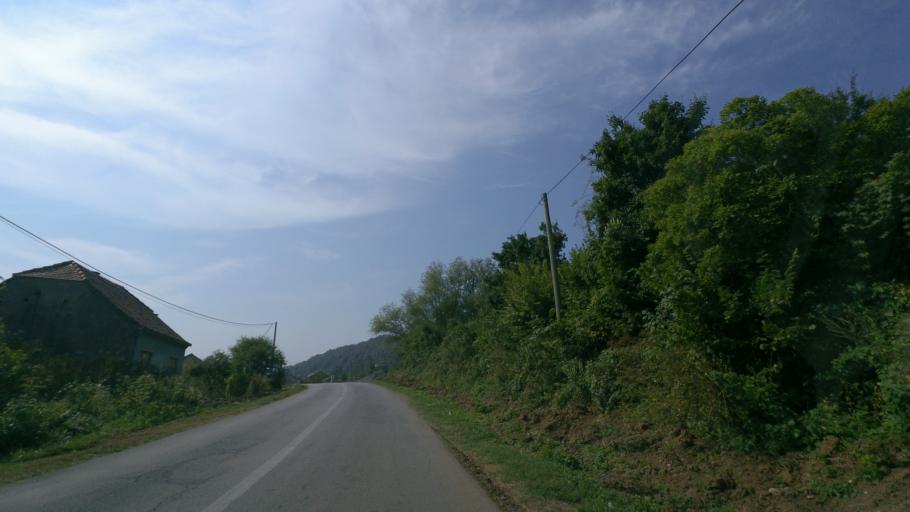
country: BA
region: Republika Srpska
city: Dobrljin
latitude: 45.1803
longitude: 16.4721
